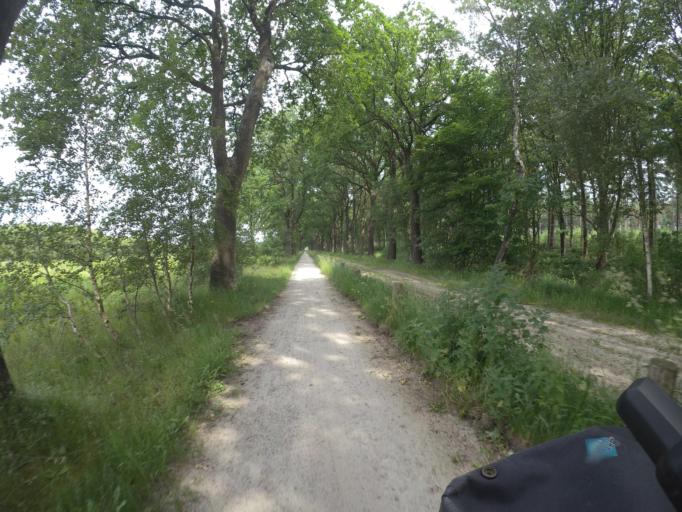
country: NL
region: Drenthe
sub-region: Gemeente Assen
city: Assen
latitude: 53.0082
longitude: 6.4411
